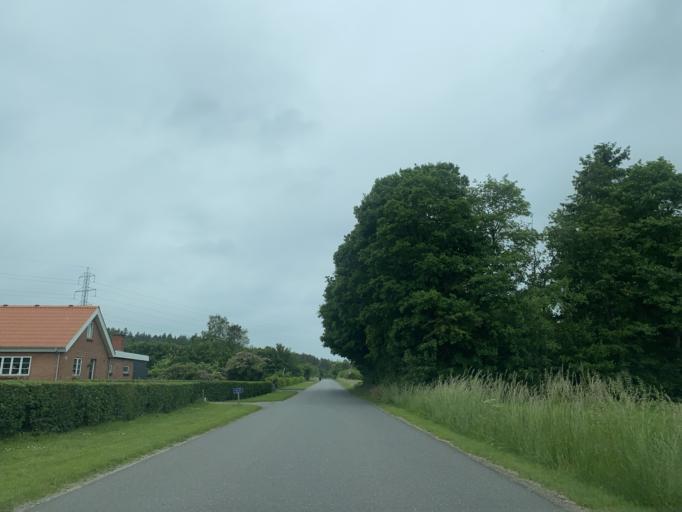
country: DK
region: Central Jutland
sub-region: Viborg Kommune
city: Bjerringbro
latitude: 56.3614
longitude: 9.6497
